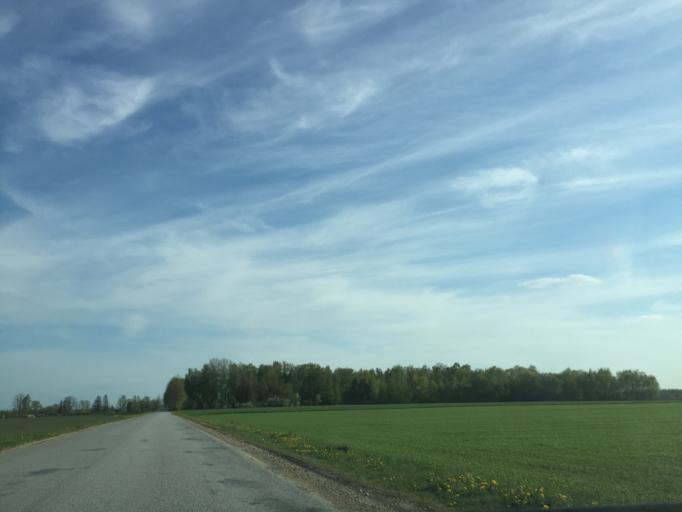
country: LV
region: Bauskas Rajons
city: Bauska
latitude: 56.3492
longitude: 24.2333
